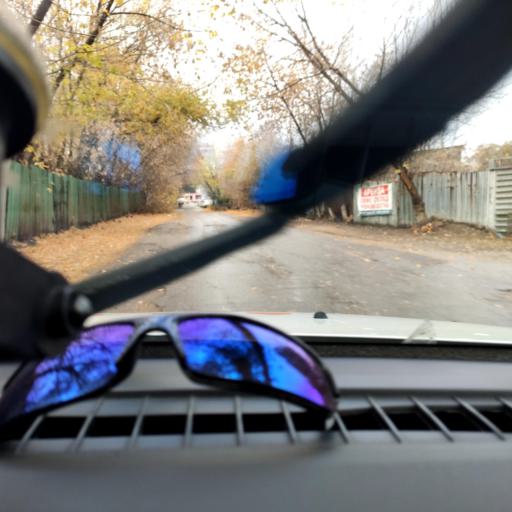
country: RU
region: Samara
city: Samara
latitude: 53.1775
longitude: 50.1949
